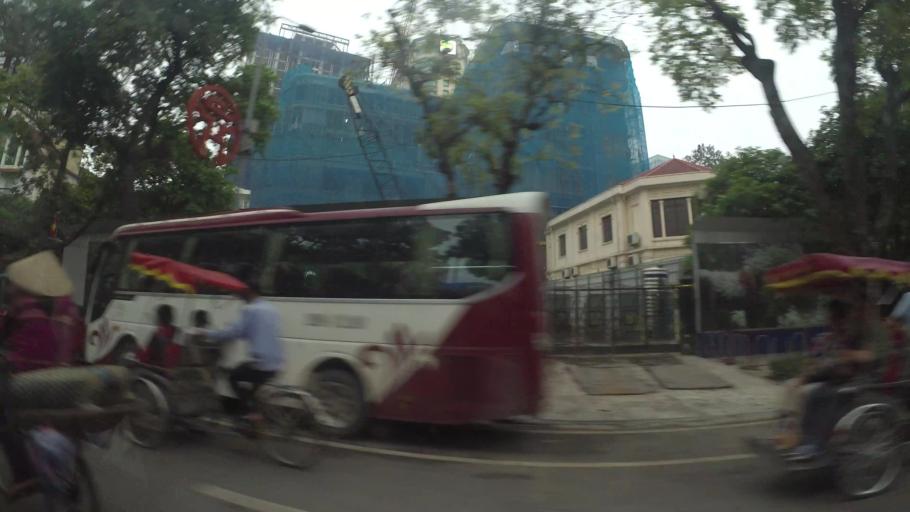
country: VN
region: Ha Noi
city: Hoan Kiem
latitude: 21.0280
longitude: 105.8563
